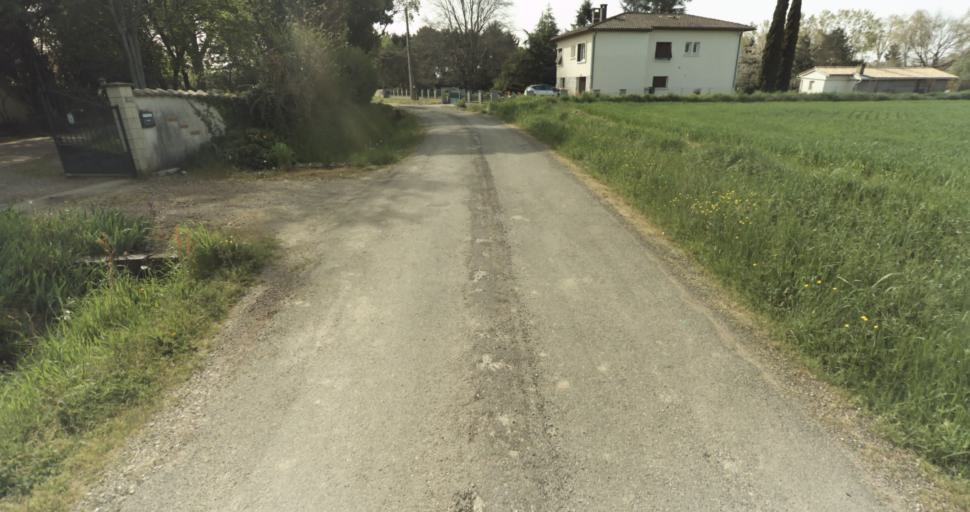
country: FR
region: Midi-Pyrenees
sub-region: Departement du Tarn-et-Garonne
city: Moissac
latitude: 44.0844
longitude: 1.0929
